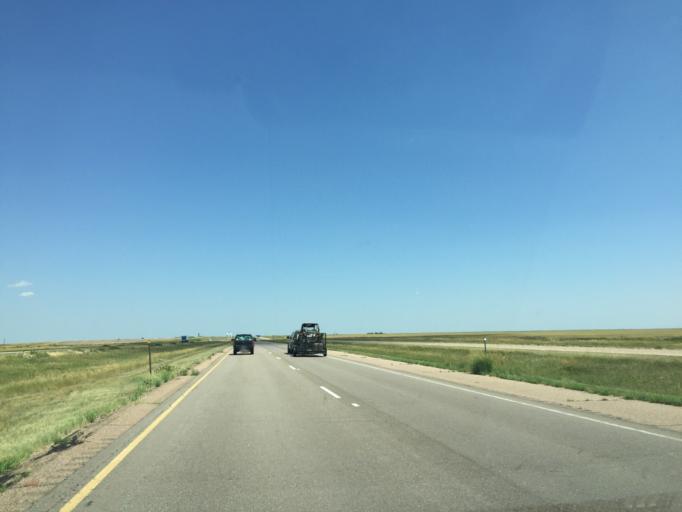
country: US
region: Colorado
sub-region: Lincoln County
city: Hugo
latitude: 39.2812
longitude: -103.3358
